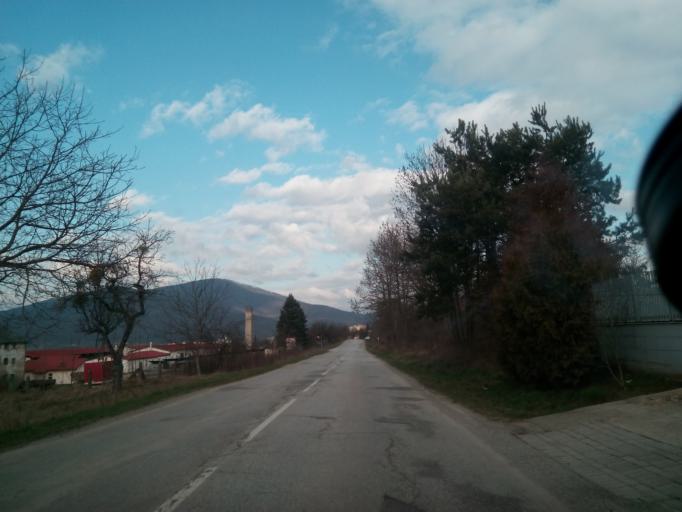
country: SK
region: Kosicky
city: Roznava
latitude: 48.6542
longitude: 20.5528
